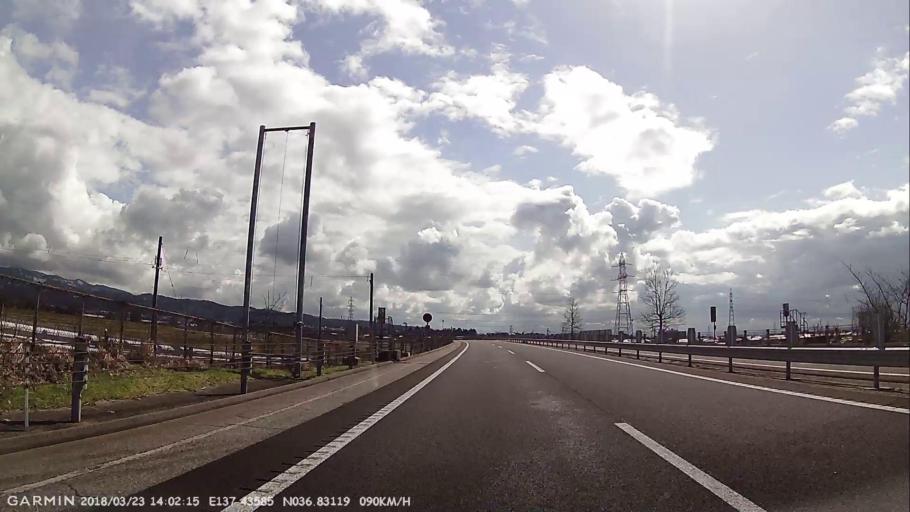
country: JP
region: Toyama
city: Uozu
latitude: 36.8305
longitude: 137.4350
